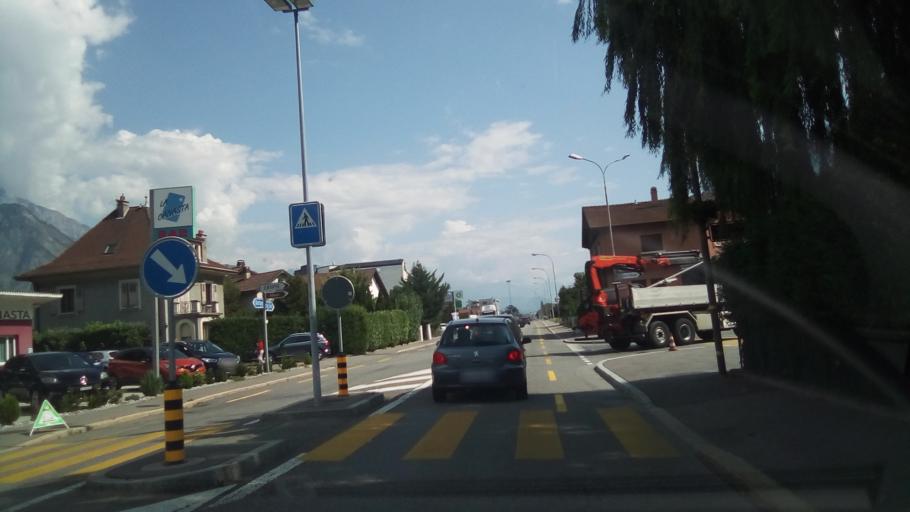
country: CH
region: Valais
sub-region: Martigny District
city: Saxon
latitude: 46.1510
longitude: 7.1786
